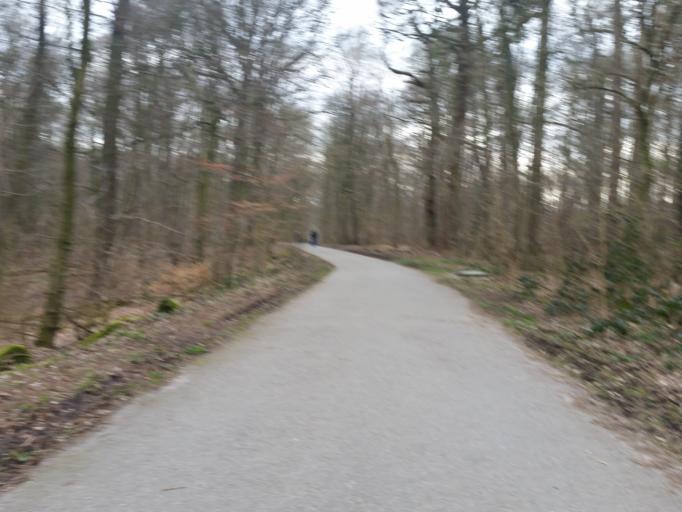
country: BE
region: Flanders
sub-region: Provincie Vlaams-Brabant
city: Sint-Genesius-Rode
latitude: 50.7892
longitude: 4.3876
